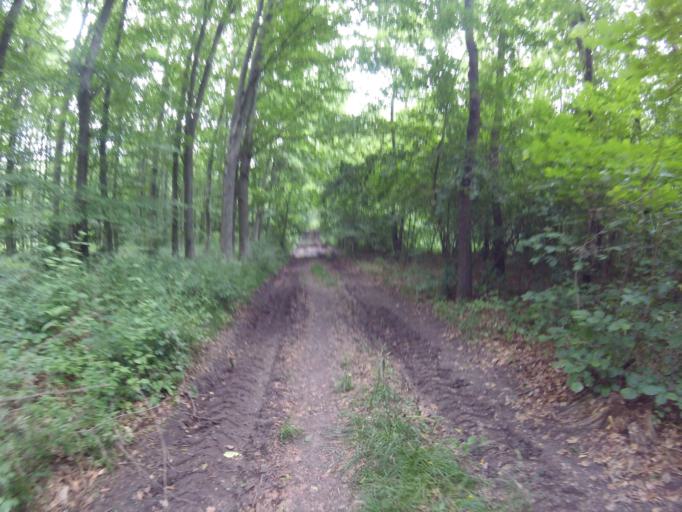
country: HU
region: Zala
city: Turje
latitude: 47.0413
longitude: 17.0194
